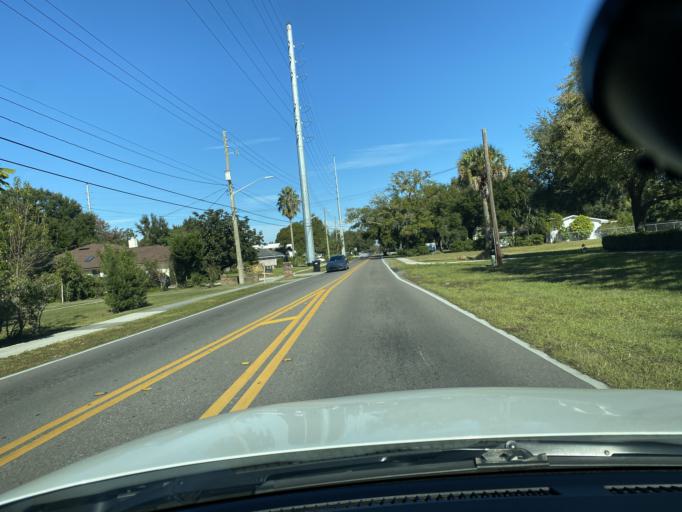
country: US
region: Florida
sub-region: Orange County
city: Conway
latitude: 28.5153
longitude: -81.3144
